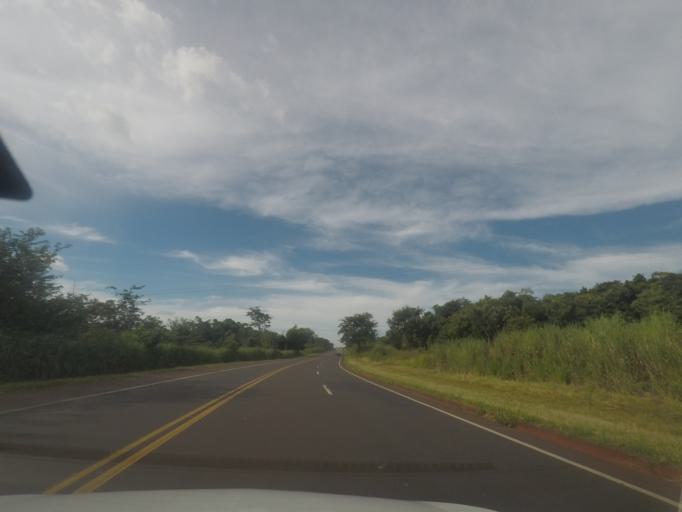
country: BR
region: Minas Gerais
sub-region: Monte Alegre De Minas
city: Monte Alegre de Minas
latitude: -19.0347
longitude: -49.0119
